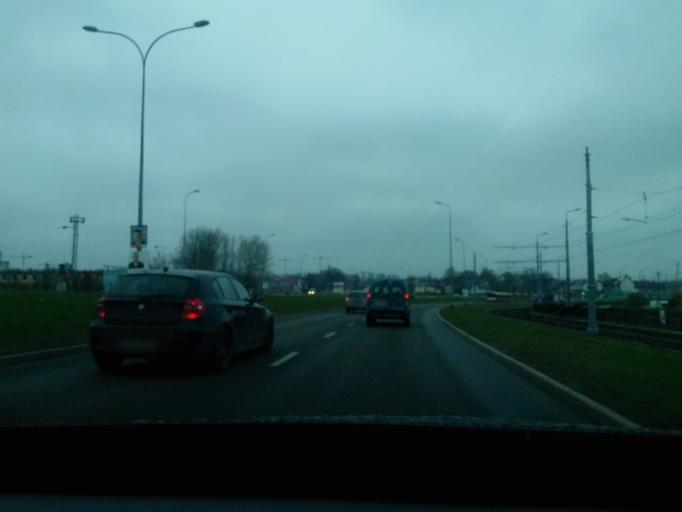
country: PL
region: Pomeranian Voivodeship
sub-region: Powiat gdanski
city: Kowale
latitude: 54.3303
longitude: 18.5972
